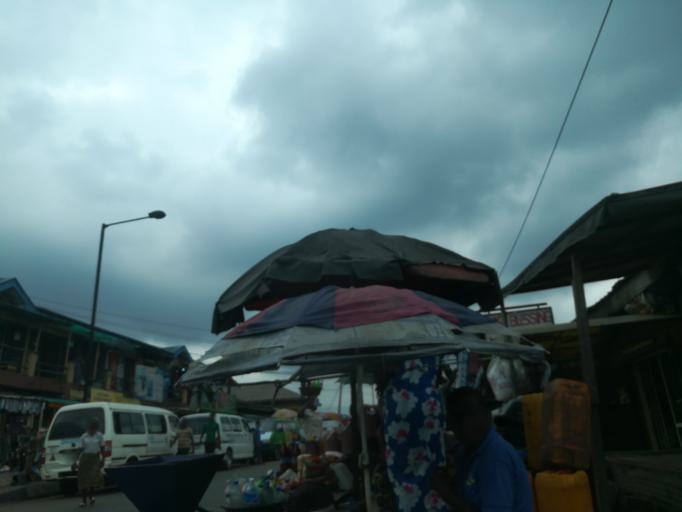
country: NG
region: Lagos
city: Ojota
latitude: 6.6088
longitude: 3.3971
